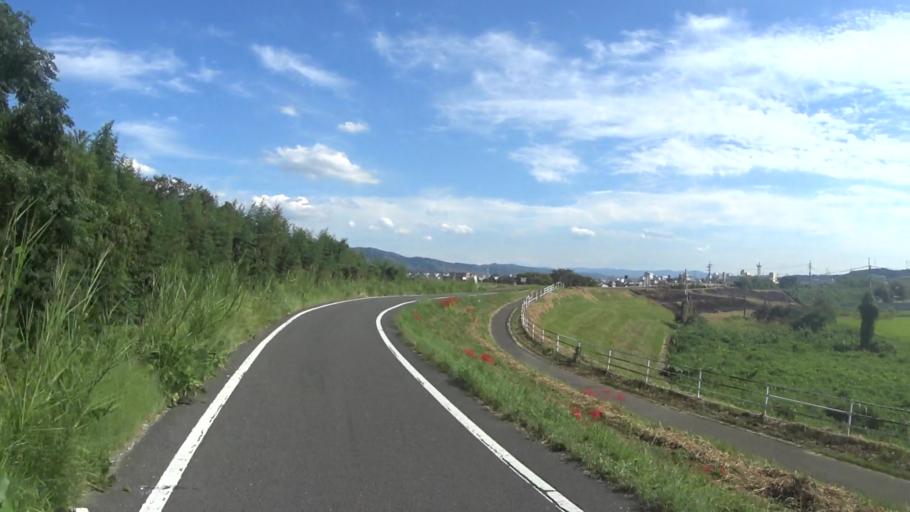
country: JP
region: Kyoto
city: Tanabe
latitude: 34.8316
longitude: 135.7640
